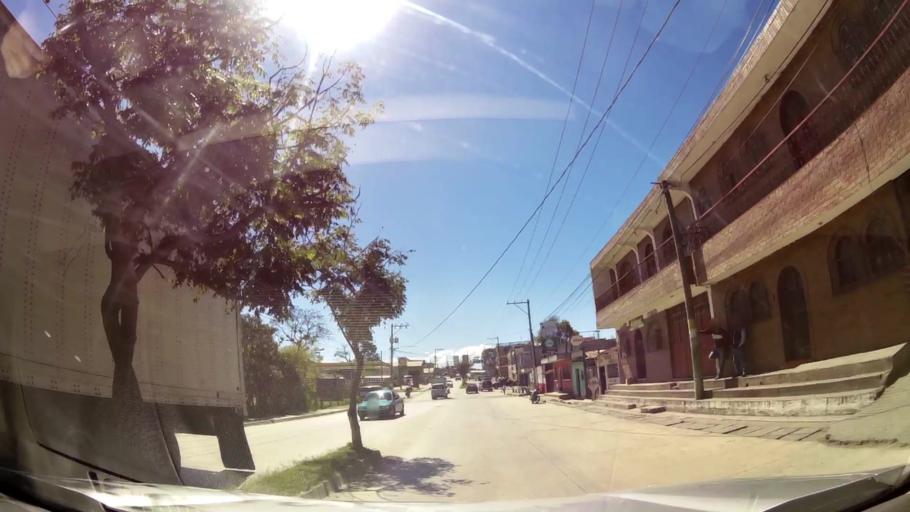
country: GT
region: Guatemala
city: San Jose Pinula
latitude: 14.5450
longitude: -90.4089
